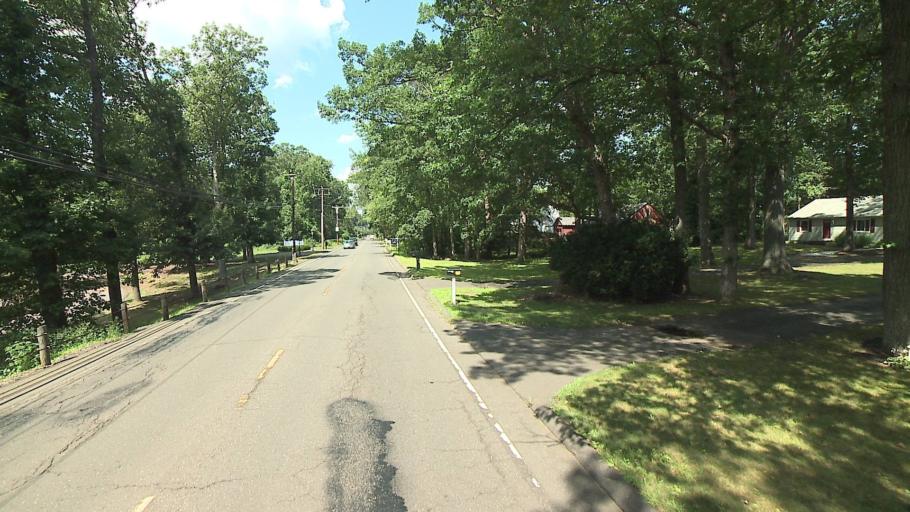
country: US
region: Connecticut
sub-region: Hartford County
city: Farmington
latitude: 41.7150
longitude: -72.8078
